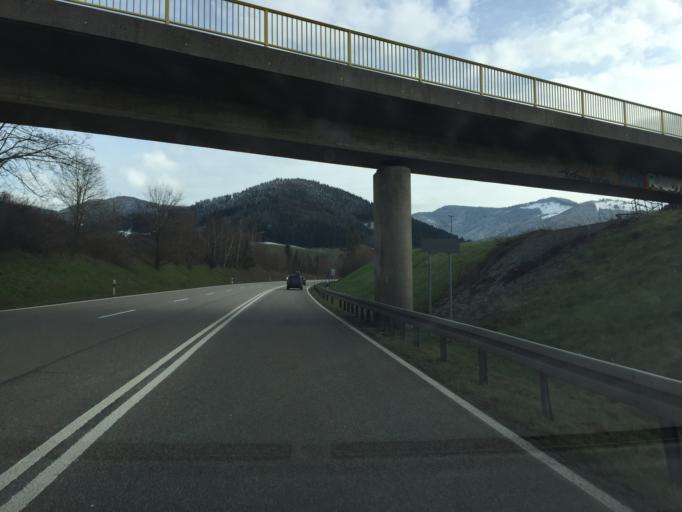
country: DE
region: Baden-Wuerttemberg
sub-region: Freiburg Region
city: Stegen
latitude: 47.9659
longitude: 7.9856
